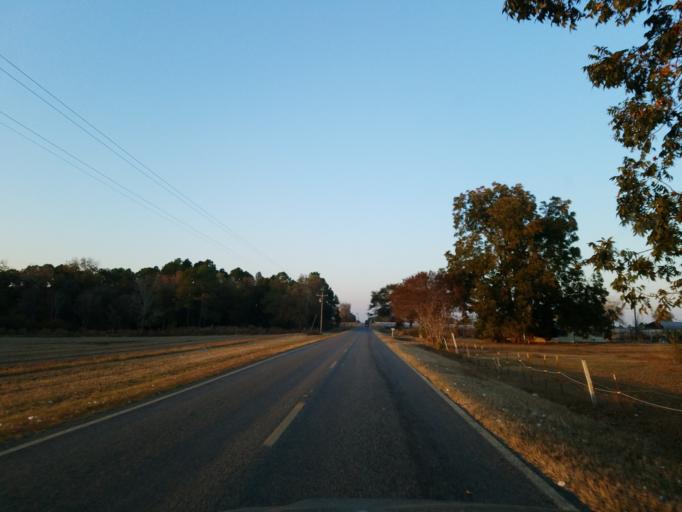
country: US
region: Georgia
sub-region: Ben Hill County
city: Fitzgerald
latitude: 31.6796
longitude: -83.3854
